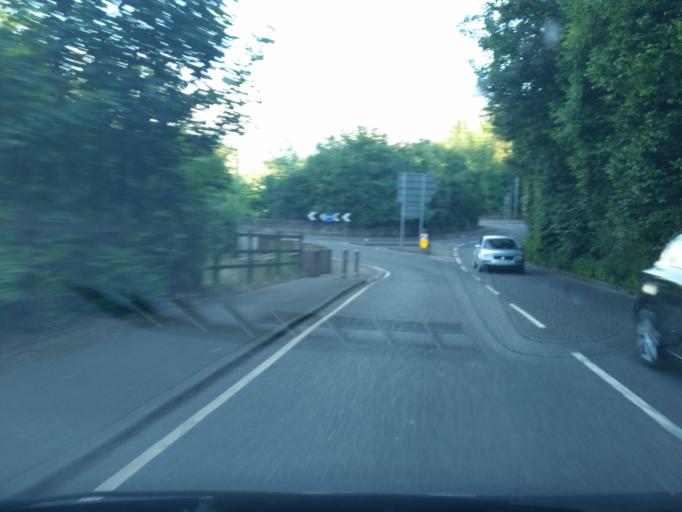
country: GB
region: Scotland
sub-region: South Lanarkshire
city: Dalserf
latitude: 55.7378
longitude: -3.9242
